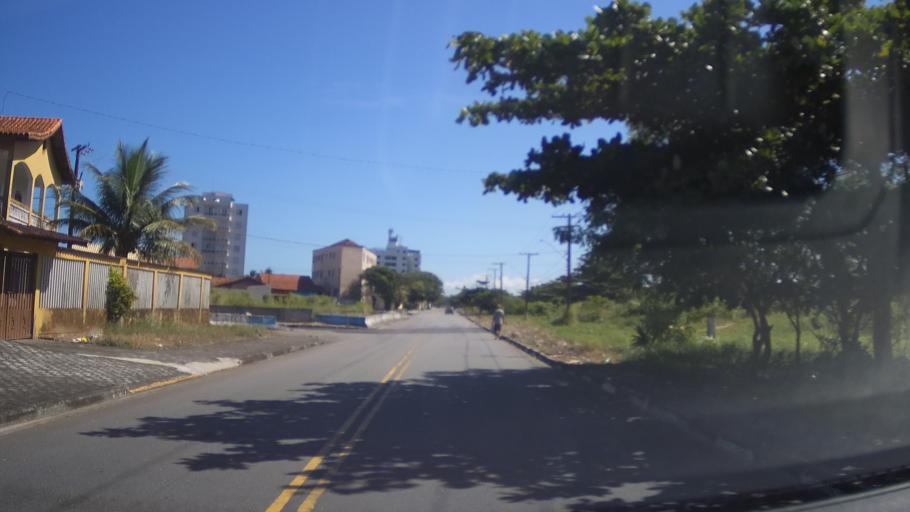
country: BR
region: Sao Paulo
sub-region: Mongagua
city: Mongagua
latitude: -24.1194
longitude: -46.6696
